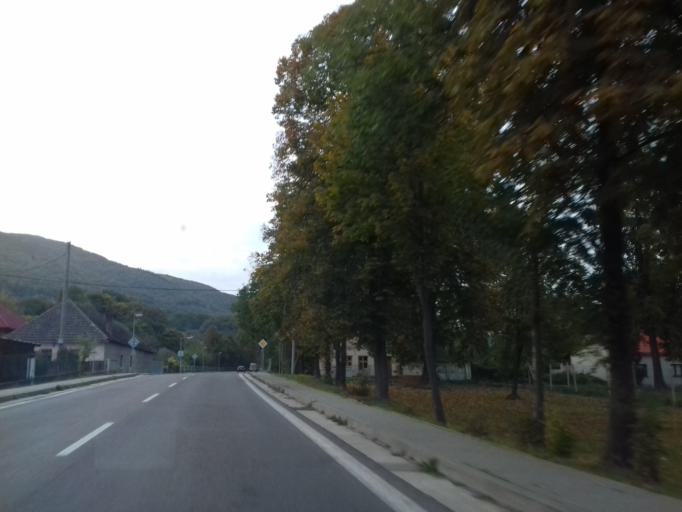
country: SK
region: Trenciansky
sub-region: Okres Trencin
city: Trencin
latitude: 48.8943
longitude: 17.9535
